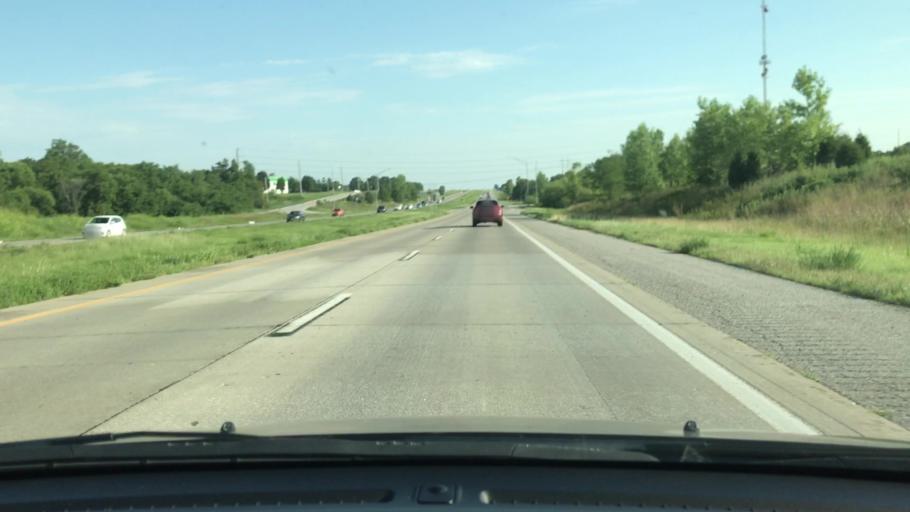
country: US
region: Missouri
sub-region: Jackson County
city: Greenwood
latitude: 38.8693
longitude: -94.3751
